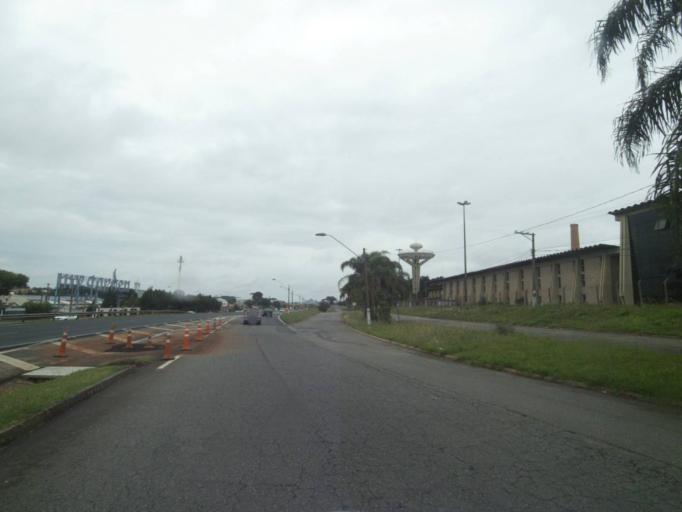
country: BR
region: Parana
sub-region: Curitiba
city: Curitiba
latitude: -25.4304
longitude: -49.3501
